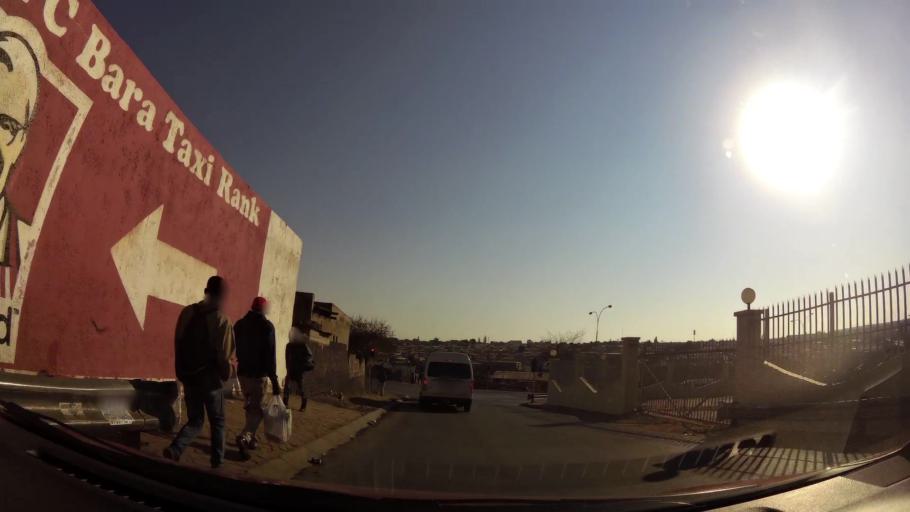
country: ZA
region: Gauteng
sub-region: City of Johannesburg Metropolitan Municipality
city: Soweto
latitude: -26.2564
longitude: 27.9408
